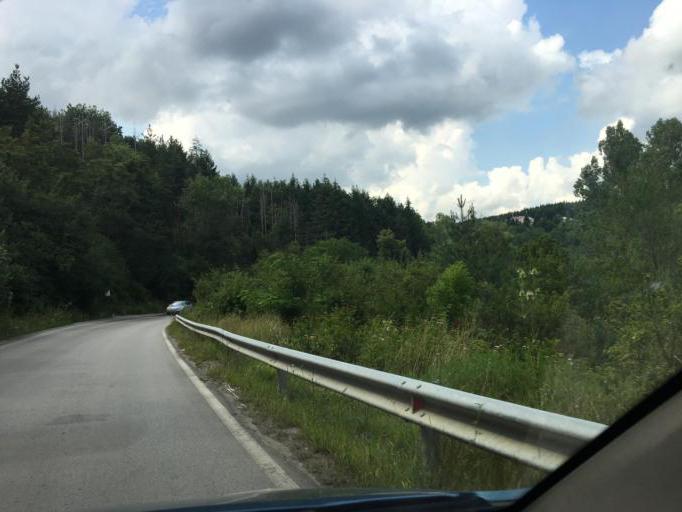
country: BG
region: Sofia-Capital
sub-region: Stolichna Obshtina
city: Sofia
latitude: 42.5942
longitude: 23.3654
